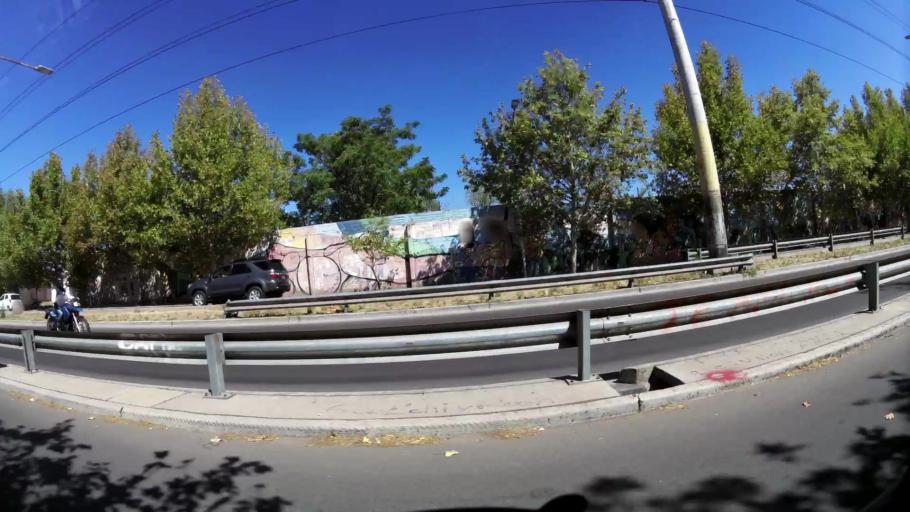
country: AR
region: Mendoza
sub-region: Departamento de Godoy Cruz
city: Godoy Cruz
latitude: -32.9216
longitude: -68.8635
